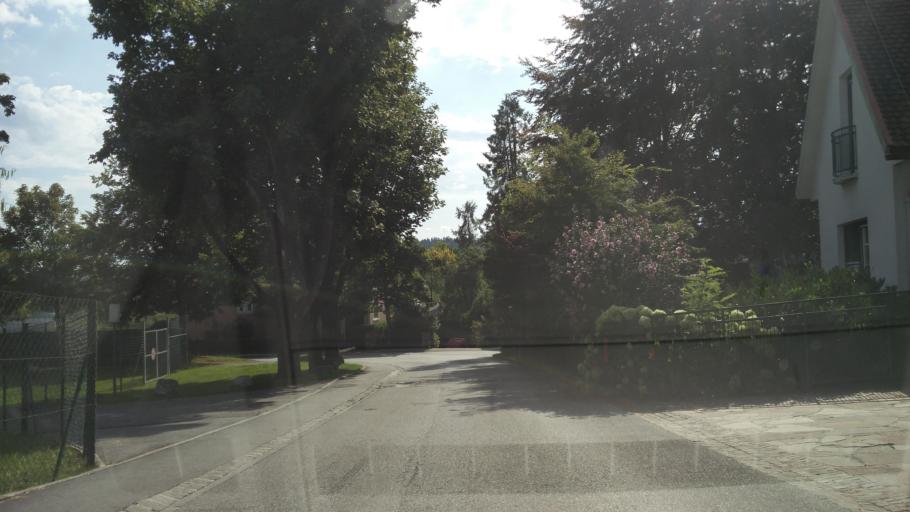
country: AT
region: Styria
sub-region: Politischer Bezirk Weiz
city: Weiz
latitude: 47.2215
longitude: 15.6314
